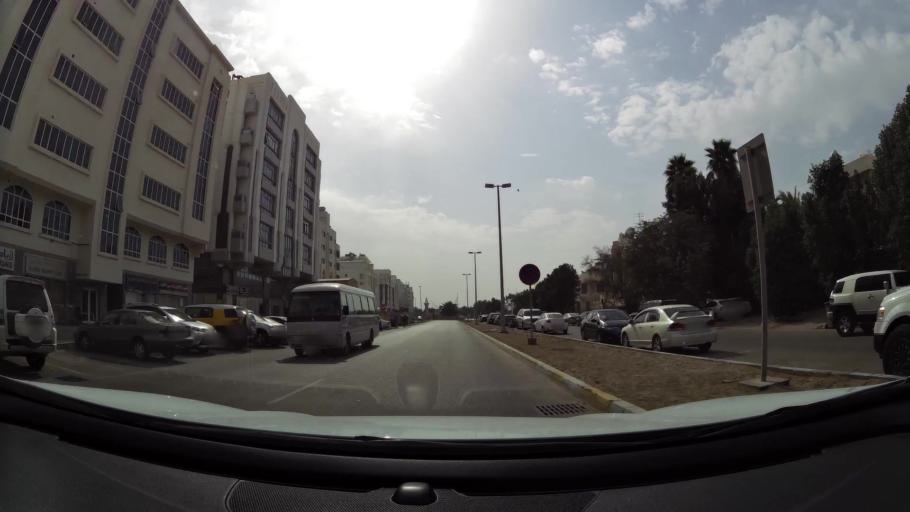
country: AE
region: Abu Dhabi
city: Abu Dhabi
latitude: 24.4499
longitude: 54.3884
